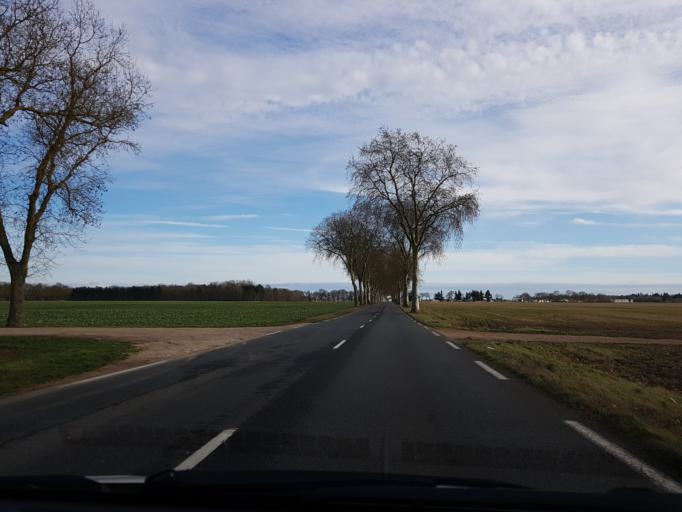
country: FR
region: Centre
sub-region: Departement du Loiret
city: Saint-Denis-en-Val
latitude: 47.8589
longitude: 1.9862
